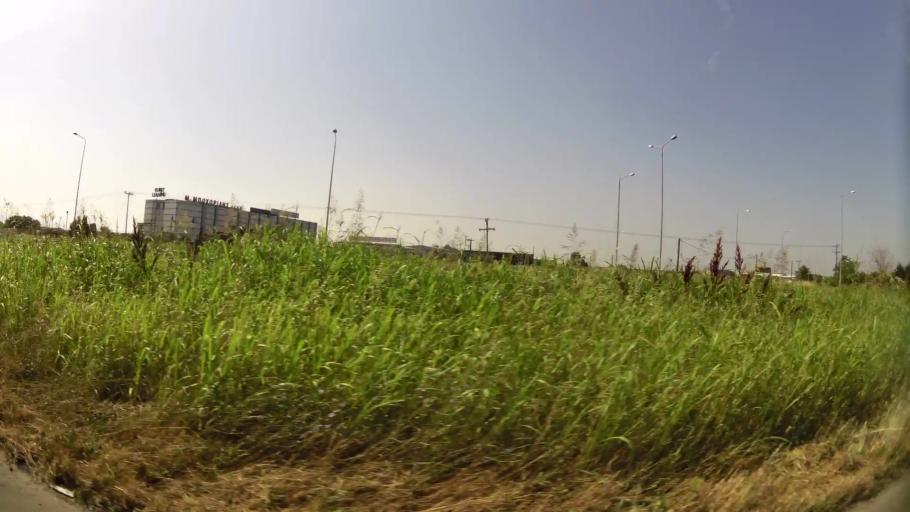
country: GR
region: Central Macedonia
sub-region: Nomos Thessalonikis
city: Sindos
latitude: 40.6512
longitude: 22.8178
